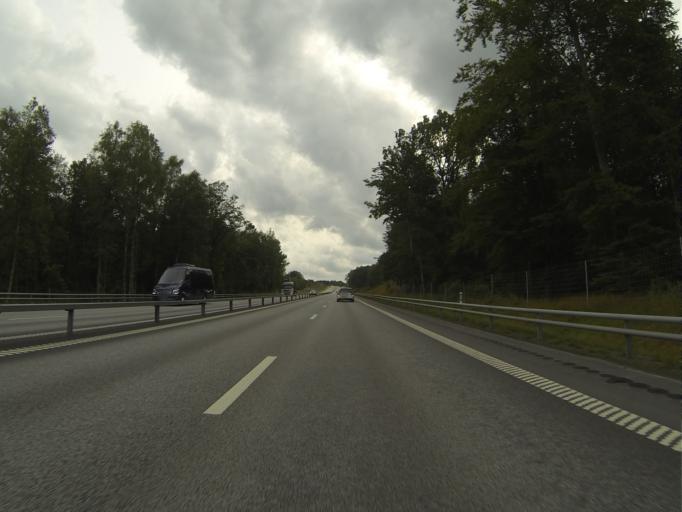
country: SE
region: Skane
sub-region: Horby Kommun
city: Hoerby
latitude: 55.9179
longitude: 13.7807
